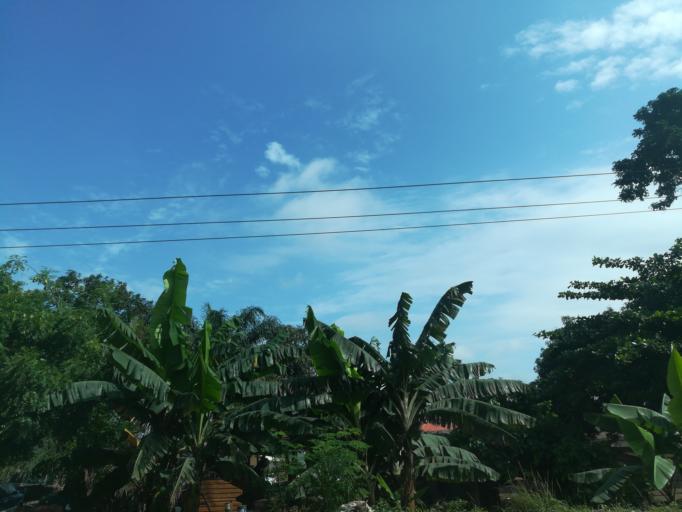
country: NG
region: Lagos
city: Ikorodu
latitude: 6.6300
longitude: 3.5148
